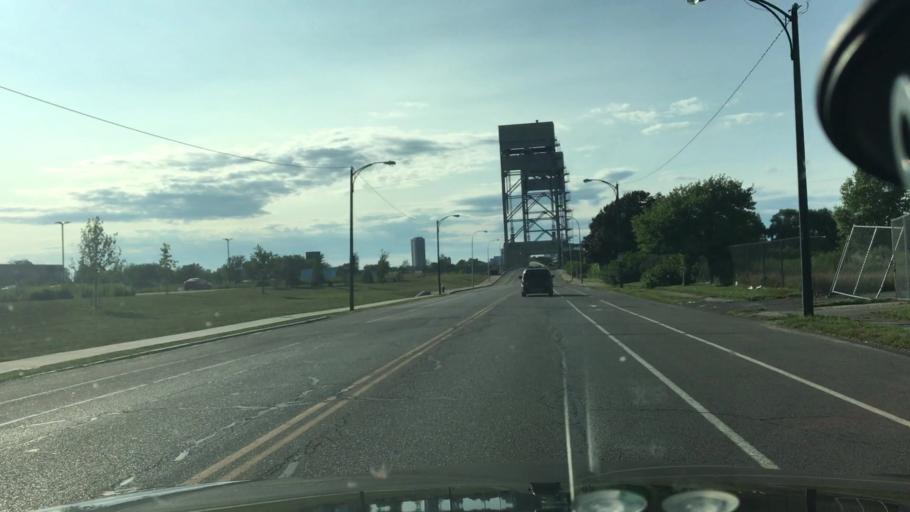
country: US
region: New York
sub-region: Erie County
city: Lackawanna
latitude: 42.8611
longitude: -78.8399
